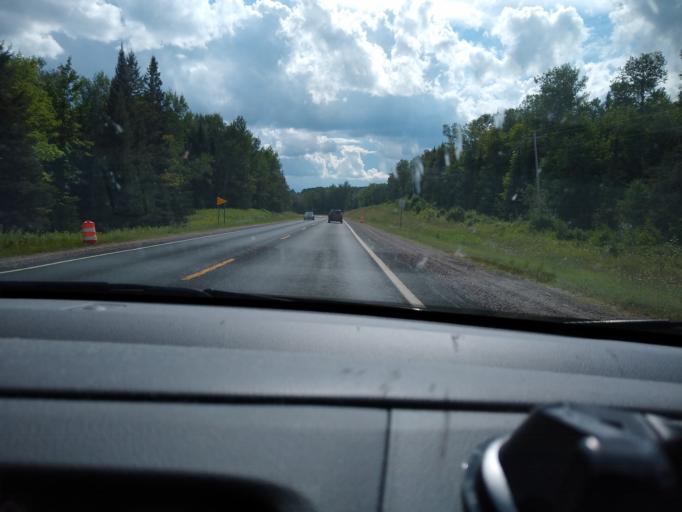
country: US
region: Michigan
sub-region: Marquette County
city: West Ishpeming
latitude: 46.2849
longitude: -88.0139
